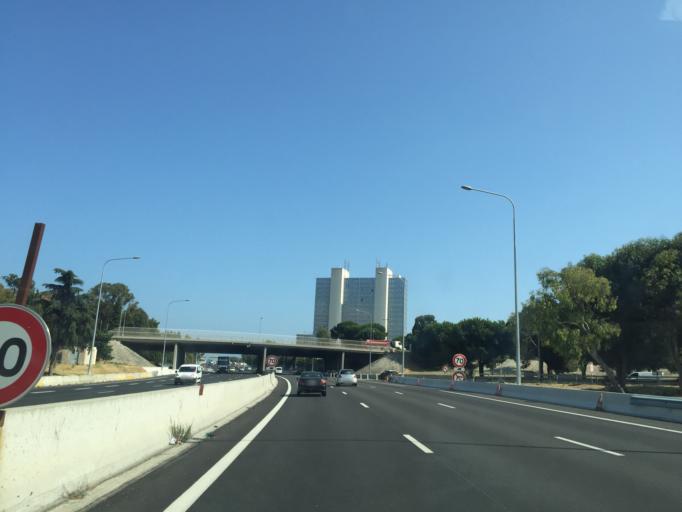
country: FR
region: Provence-Alpes-Cote d'Azur
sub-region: Departement des Alpes-Maritimes
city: Saint-Laurent-du-Var
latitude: 43.6760
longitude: 7.1958
